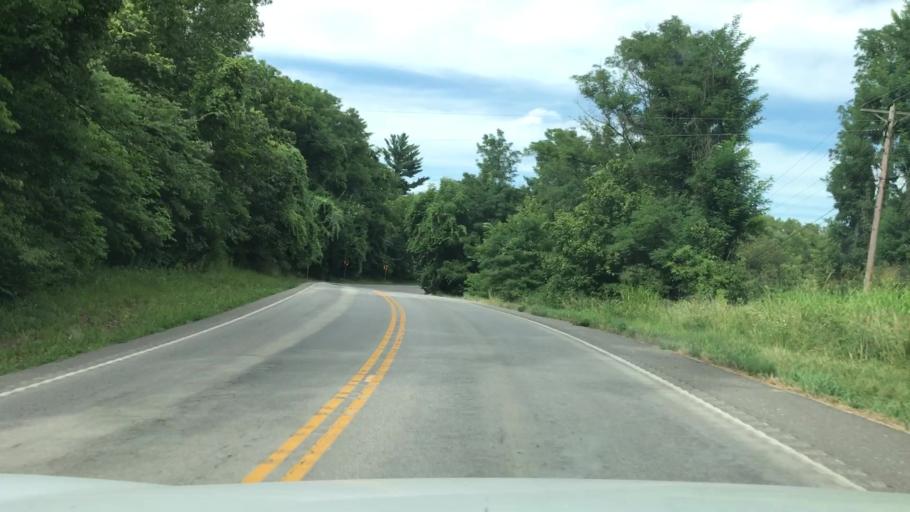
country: US
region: Missouri
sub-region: Saint Charles County
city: Weldon Spring
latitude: 38.6634
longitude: -90.7409
